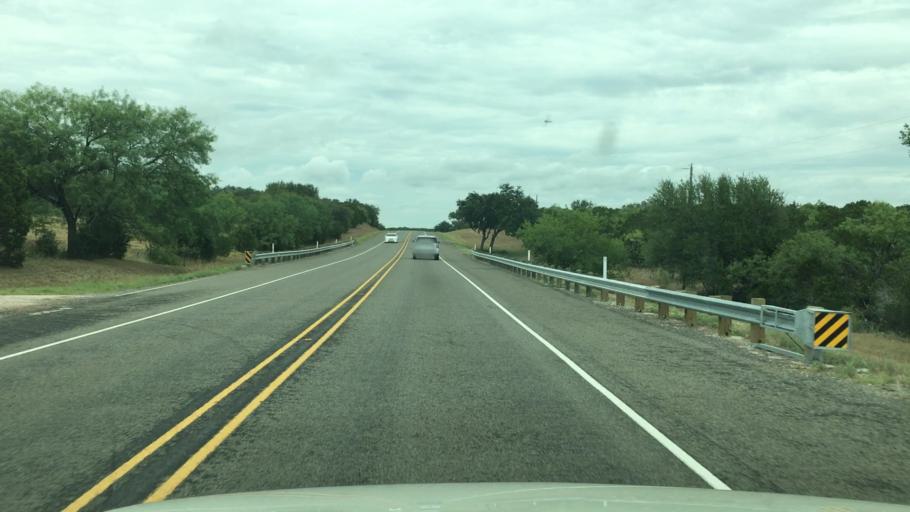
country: US
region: Texas
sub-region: Burnet County
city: Granite Shoals
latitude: 30.5414
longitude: -98.4500
